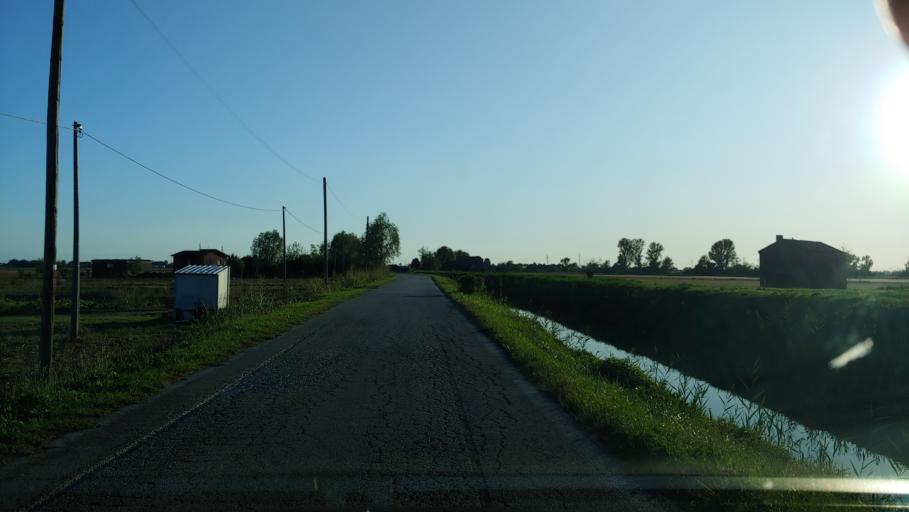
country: IT
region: Veneto
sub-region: Provincia di Rovigo
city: Pettorazza Grimani
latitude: 45.0802
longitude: 12.0041
